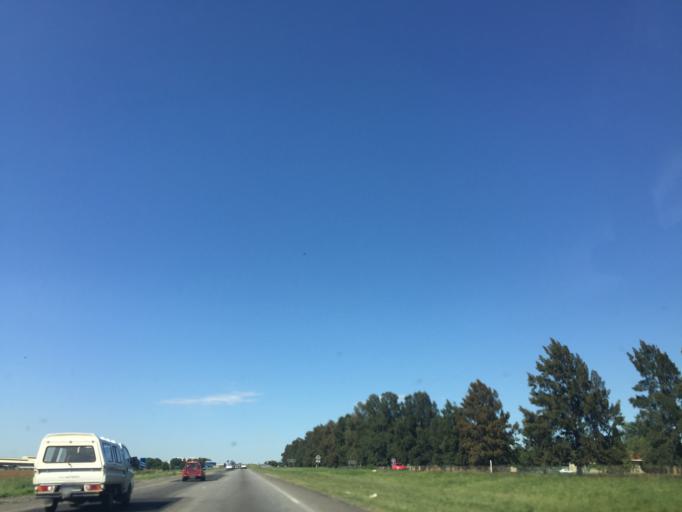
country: ZA
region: Gauteng
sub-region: Sedibeng District Municipality
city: Vereeniging
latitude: -26.6360
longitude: 27.9523
